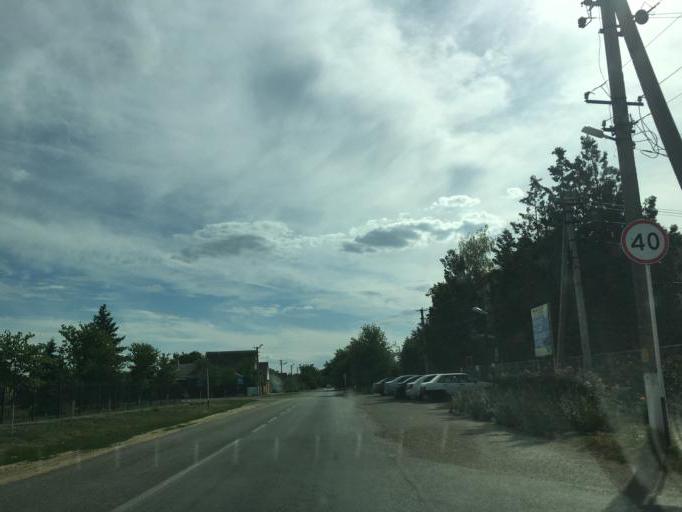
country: RU
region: Krasnodarskiy
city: Kushchevskaya
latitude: 46.5529
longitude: 39.6247
